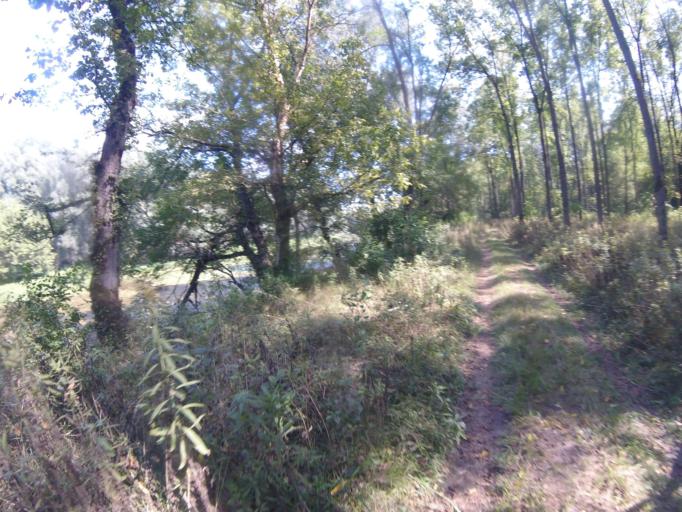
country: HU
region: Bacs-Kiskun
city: Baja
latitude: 46.1987
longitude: 18.8678
